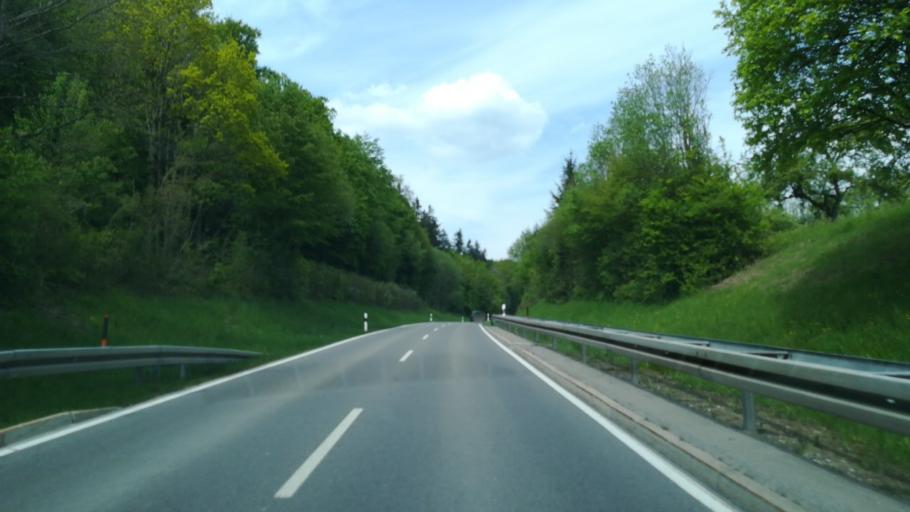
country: DE
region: Baden-Wuerttemberg
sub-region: Freiburg Region
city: Stockach
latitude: 47.8769
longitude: 9.0364
